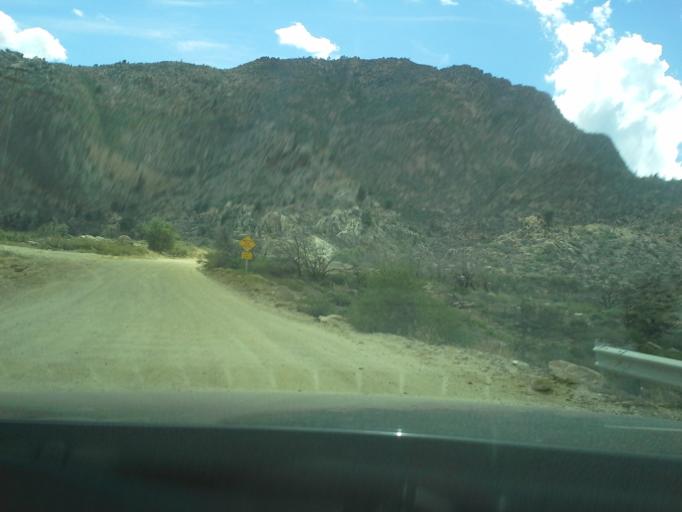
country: US
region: Arizona
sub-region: Yavapai County
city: Mayer
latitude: 34.2561
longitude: -112.2972
